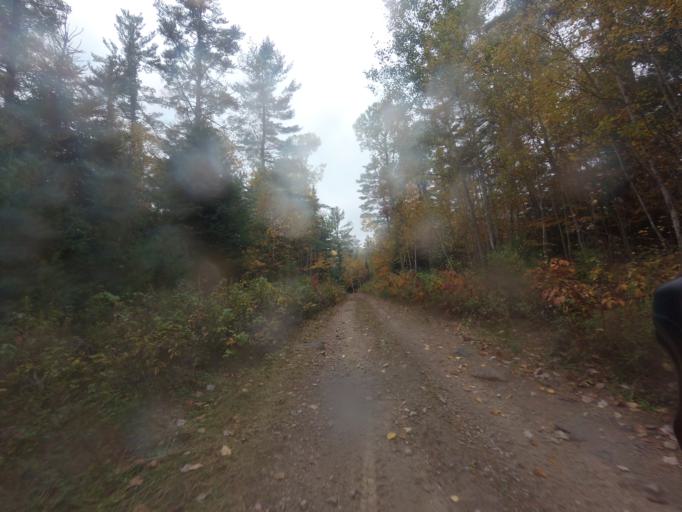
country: CA
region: Ontario
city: Petawawa
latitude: 45.7822
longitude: -77.3829
